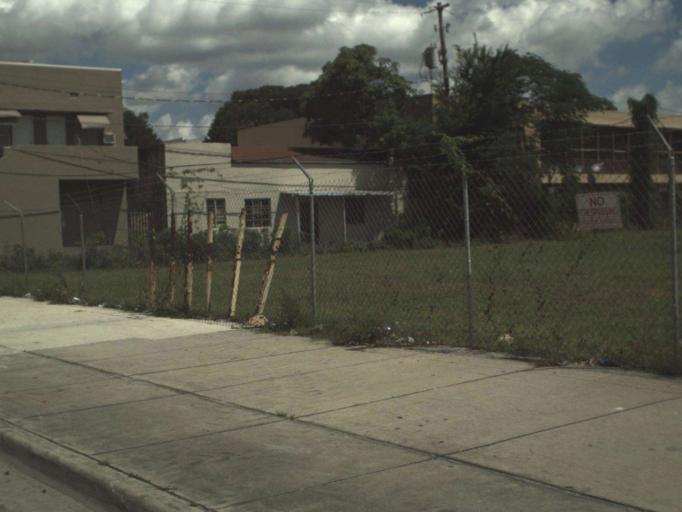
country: US
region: Florida
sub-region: Miami-Dade County
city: Miami
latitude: 25.7729
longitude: -80.2077
